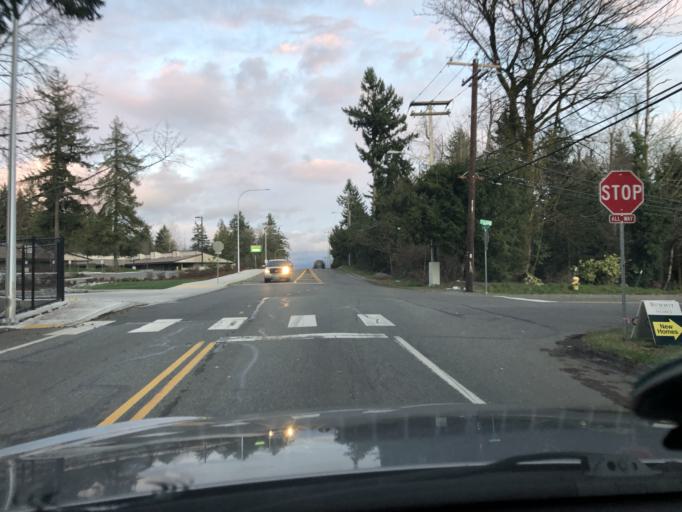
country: US
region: Washington
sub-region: King County
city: Lakeland North
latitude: 47.3187
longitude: -122.2659
